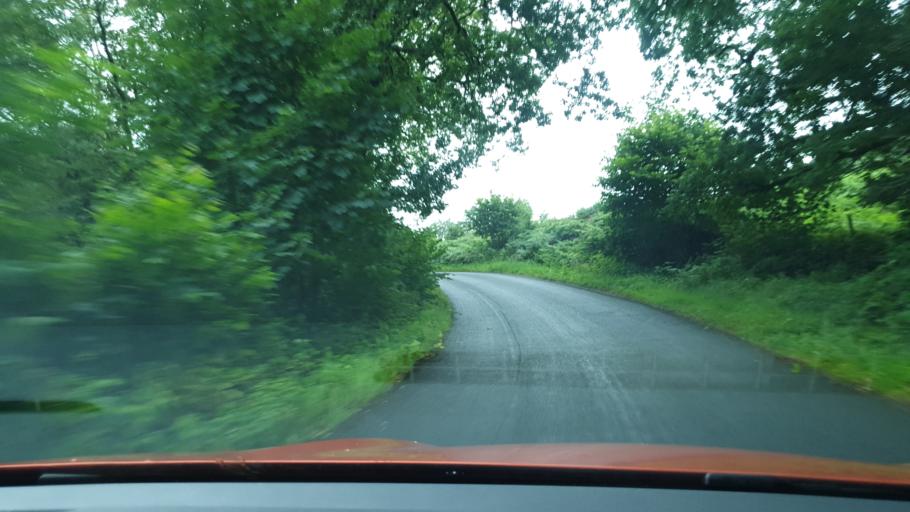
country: GB
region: England
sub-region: Cumbria
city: Seascale
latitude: 54.4129
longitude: -3.3592
